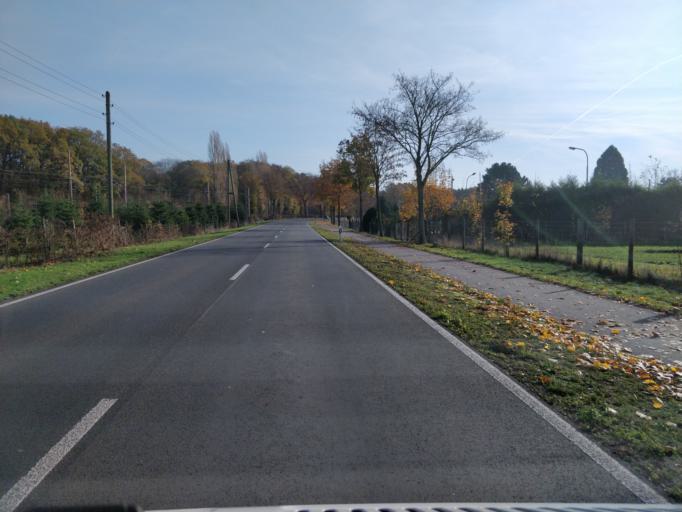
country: DE
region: North Rhine-Westphalia
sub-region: Regierungsbezirk Dusseldorf
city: Mehrhoog
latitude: 51.7639
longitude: 6.4676
